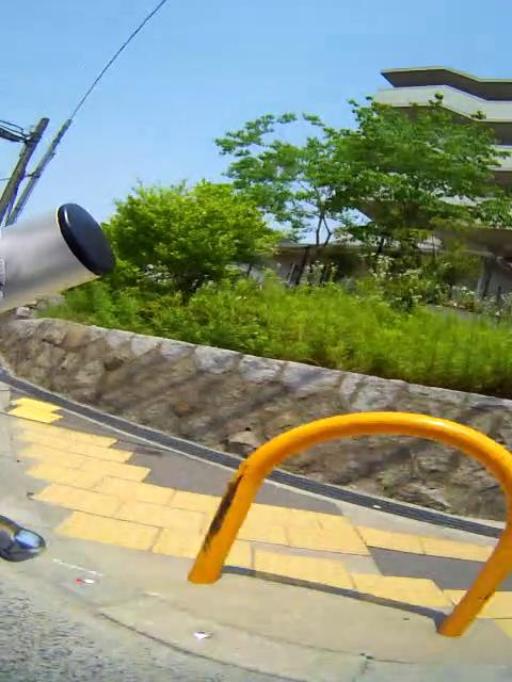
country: JP
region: Osaka
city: Suita
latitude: 34.7639
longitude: 135.5122
